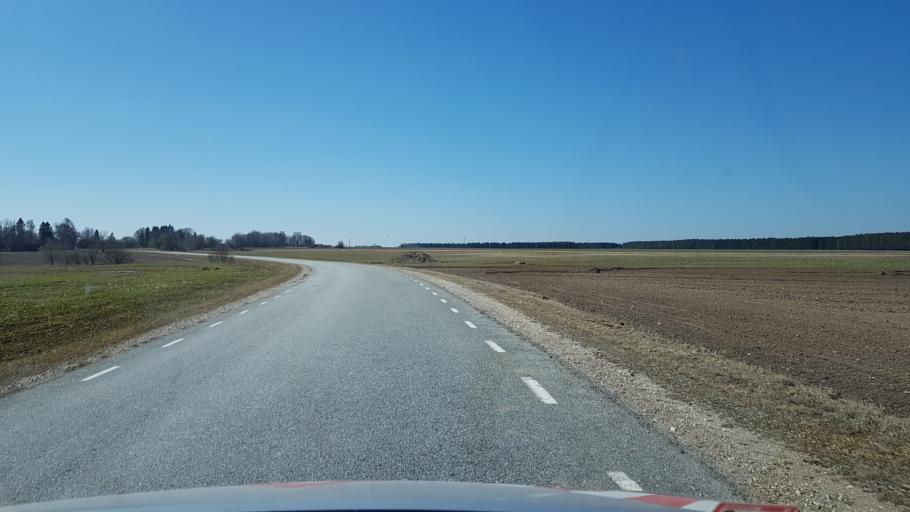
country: EE
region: Laeaene-Virumaa
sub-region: Rakke vald
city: Rakke
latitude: 59.0417
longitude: 26.3540
